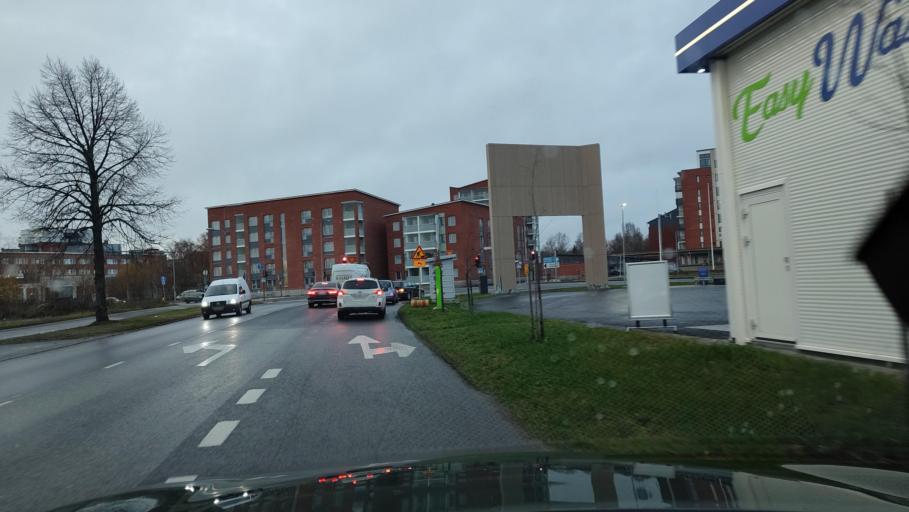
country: FI
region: Ostrobothnia
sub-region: Vaasa
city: Vaasa
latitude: 63.0991
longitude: 21.6340
